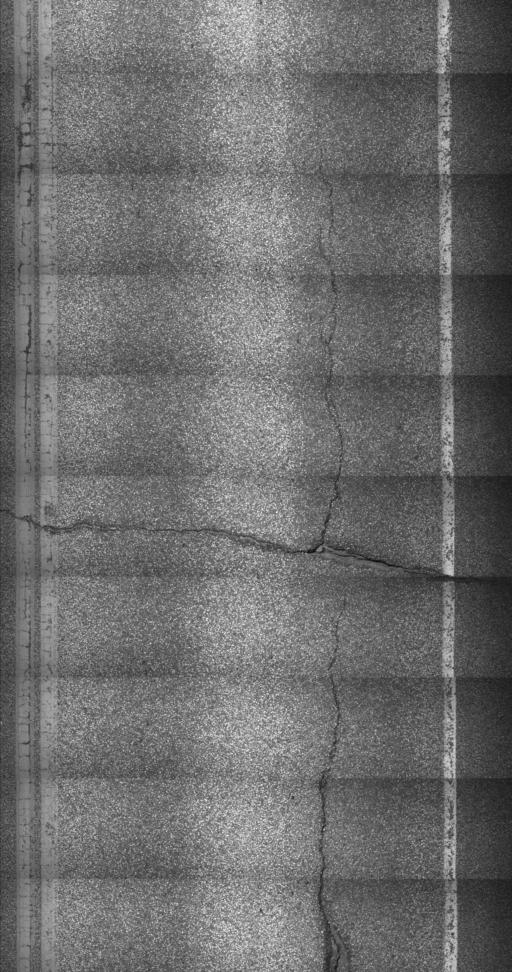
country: US
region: Vermont
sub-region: Lamoille County
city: Morristown
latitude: 44.5103
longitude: -72.7647
